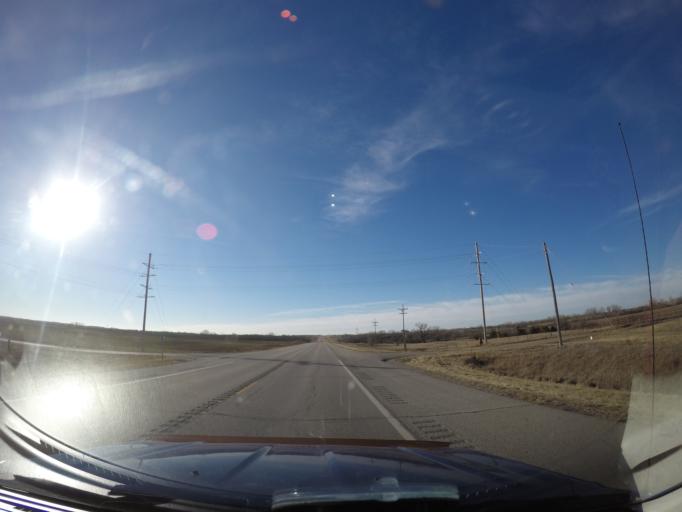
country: US
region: Kansas
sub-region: Marion County
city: Hillsboro
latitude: 38.3624
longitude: -97.3165
